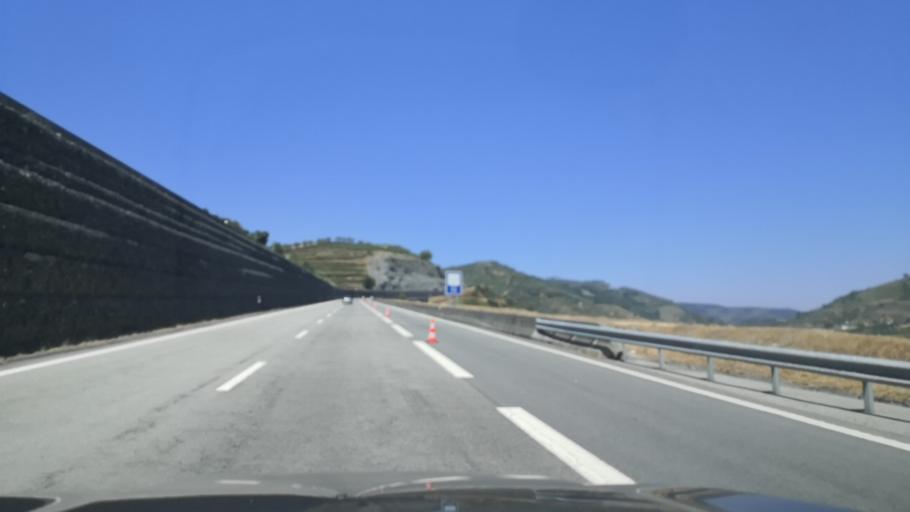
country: PT
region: Vila Real
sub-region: Peso da Regua
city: Peso da Regua
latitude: 41.1775
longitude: -7.7517
